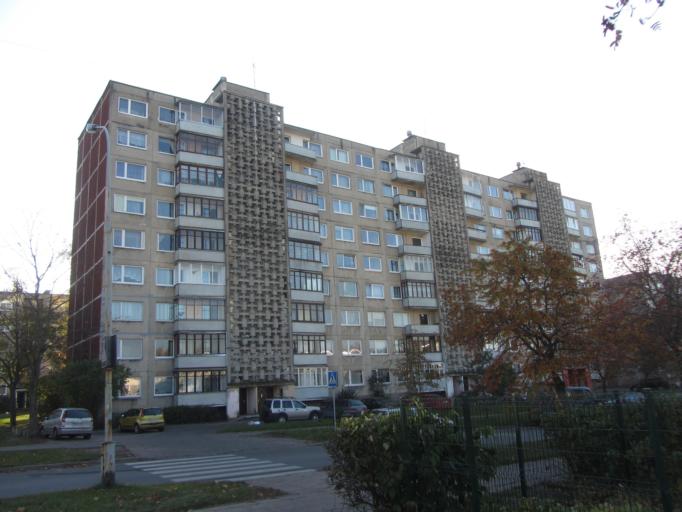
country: LT
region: Vilnius County
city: Lazdynai
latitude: 54.6862
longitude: 25.2016
